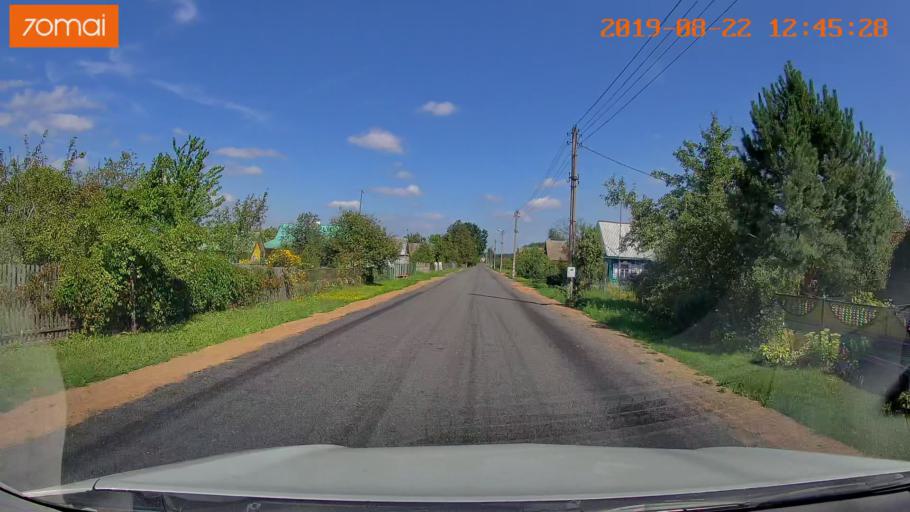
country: BY
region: Minsk
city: Prawdzinski
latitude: 53.4577
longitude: 27.6199
